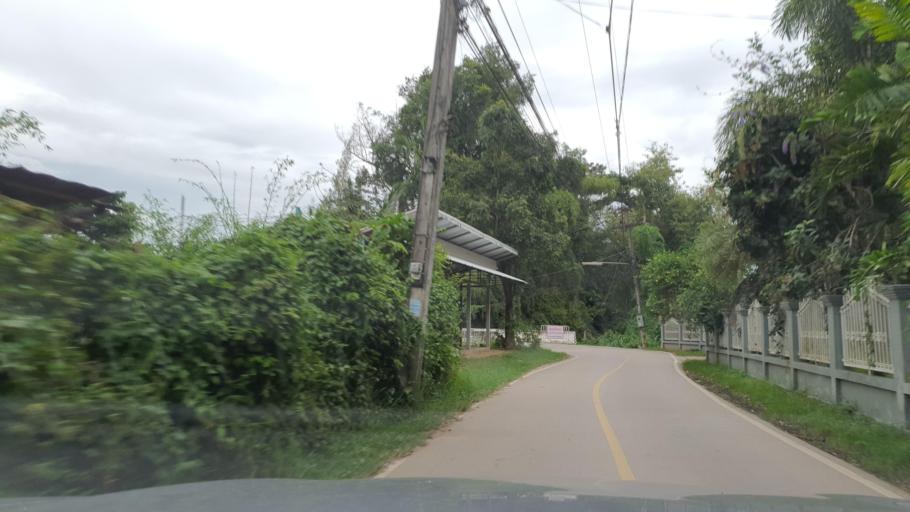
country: TH
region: Chiang Mai
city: San Sai
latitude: 18.9342
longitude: 98.9309
